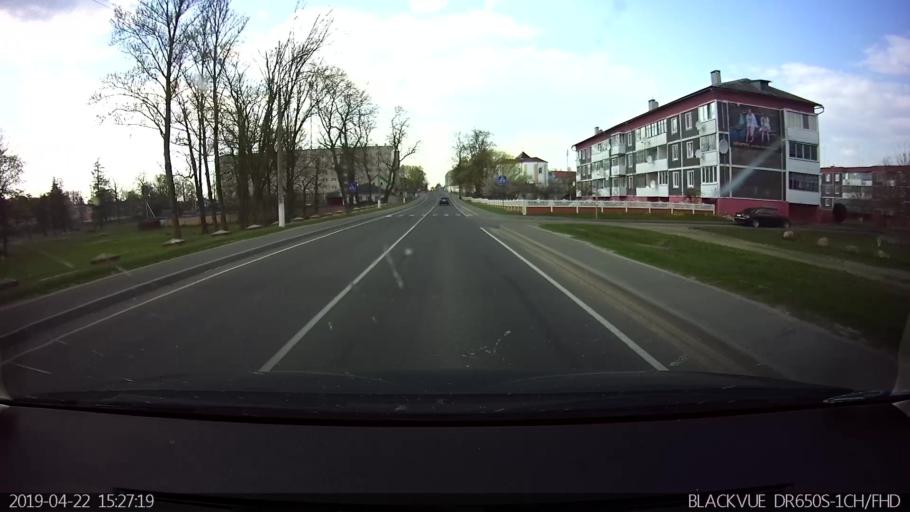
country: BY
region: Brest
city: Vysokaye
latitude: 52.3700
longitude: 23.3729
